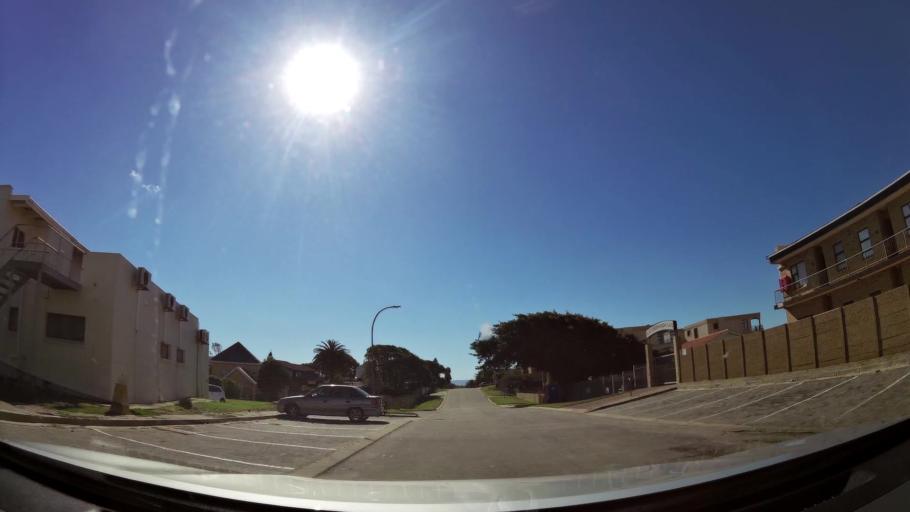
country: ZA
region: Eastern Cape
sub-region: Cacadu District Municipality
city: Jeffrey's Bay
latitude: -34.0517
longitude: 24.9237
